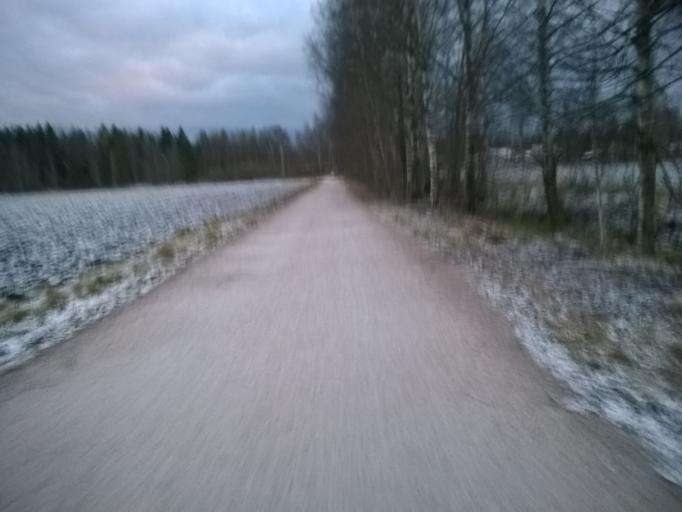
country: FI
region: Uusimaa
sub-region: Helsinki
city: Helsinki
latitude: 60.2504
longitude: 24.9080
